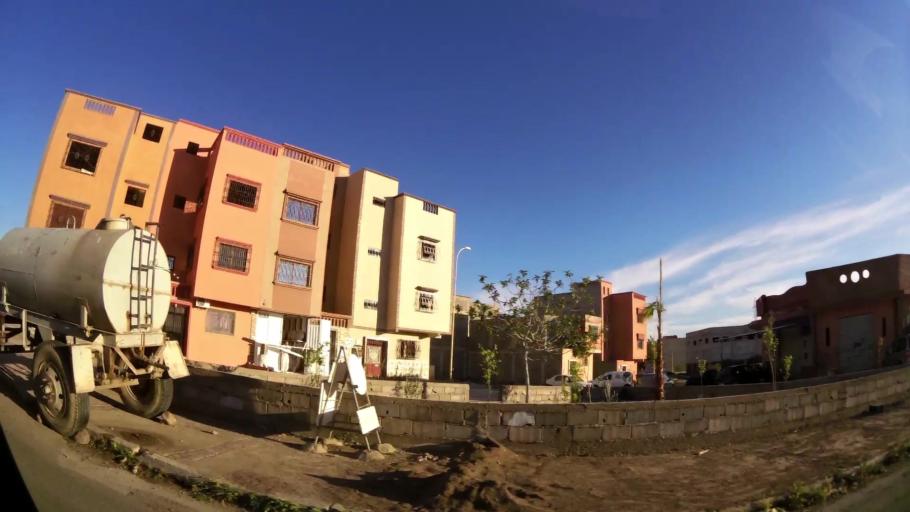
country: MA
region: Marrakech-Tensift-Al Haouz
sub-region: Marrakech
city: Marrakesh
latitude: 31.7456
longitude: -8.1166
